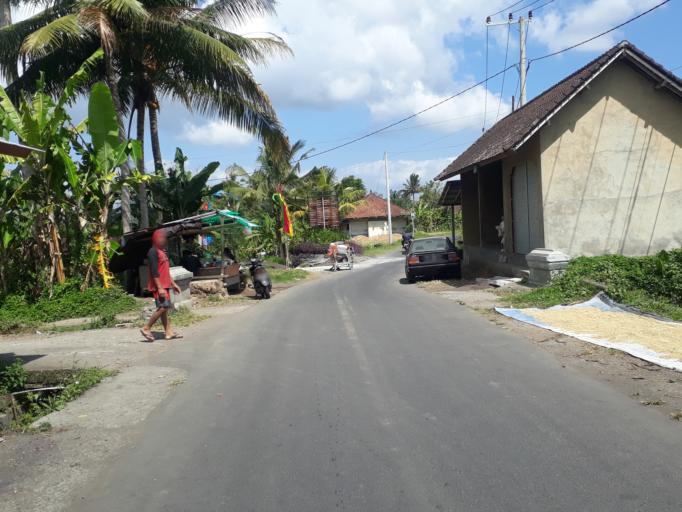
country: ID
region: Bali
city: Banjar Wangsian
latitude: -8.4728
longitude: 115.4439
